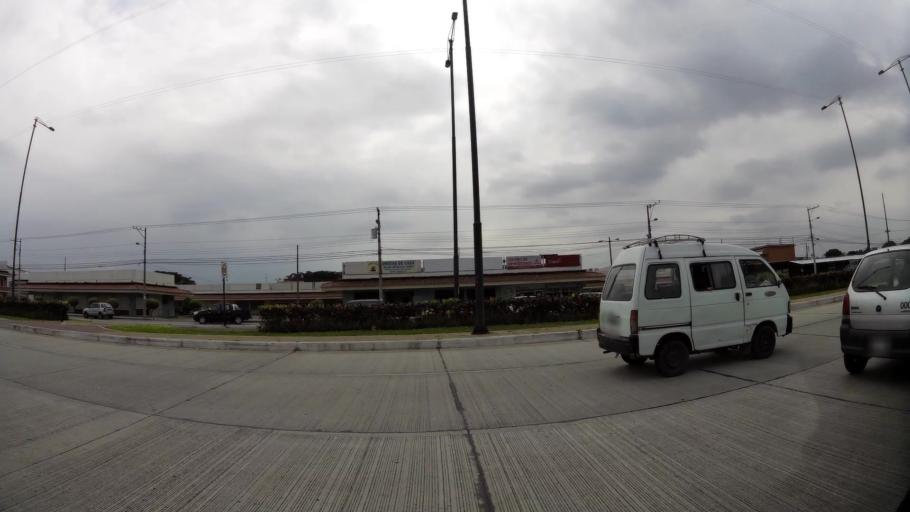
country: EC
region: Guayas
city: Eloy Alfaro
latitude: -2.1180
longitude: -79.9003
